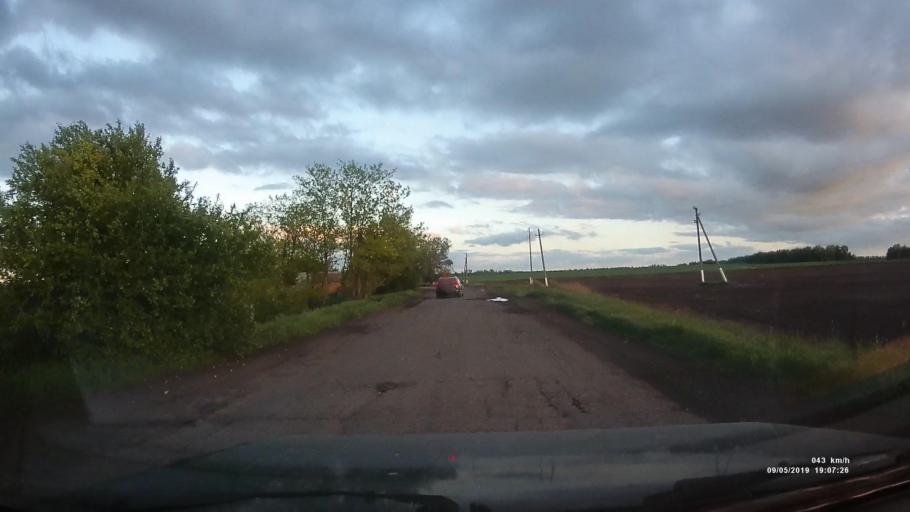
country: RU
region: Krasnodarskiy
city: Kanelovskaya
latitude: 46.7341
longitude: 39.1977
